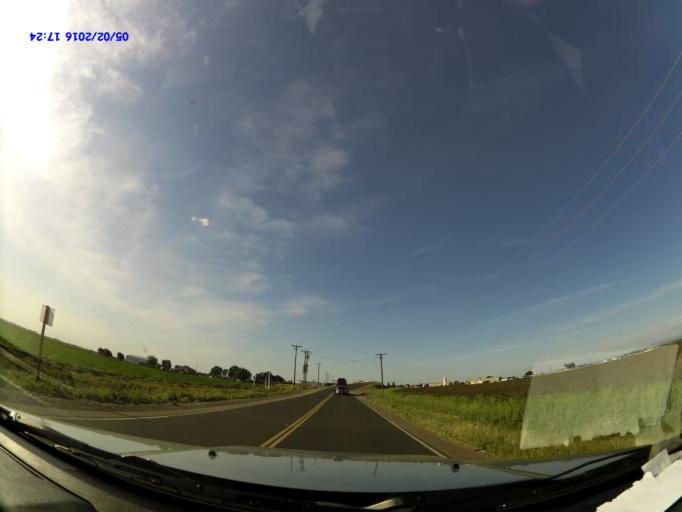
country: US
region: California
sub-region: San Joaquin County
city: Manteca
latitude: 37.8852
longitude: -121.1469
